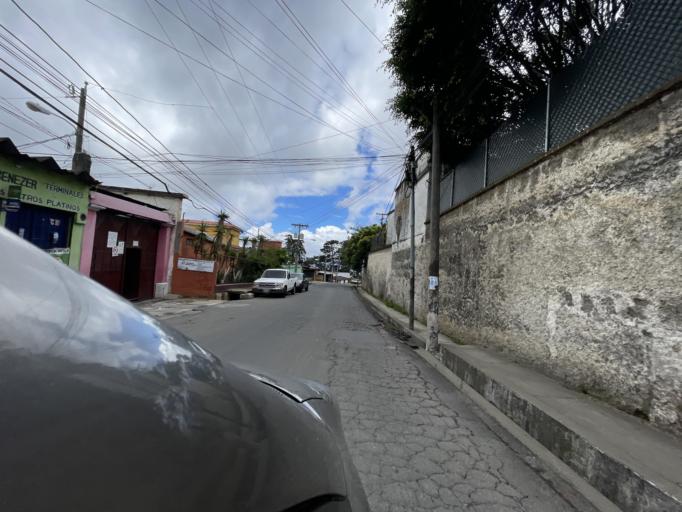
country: GT
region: Guatemala
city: Mixco
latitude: 14.6353
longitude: -90.6172
